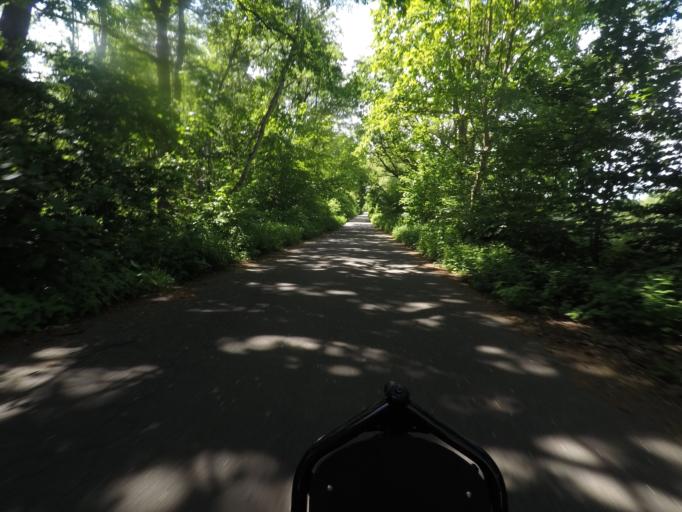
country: DE
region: Schleswig-Holstein
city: Stapelfeld
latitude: 53.6273
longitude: 10.1906
